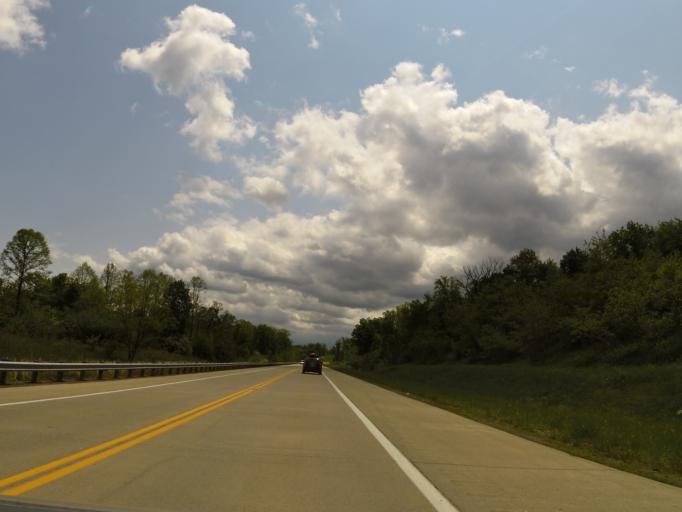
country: US
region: Ohio
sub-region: Athens County
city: Athens
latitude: 39.2119
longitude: -82.0613
